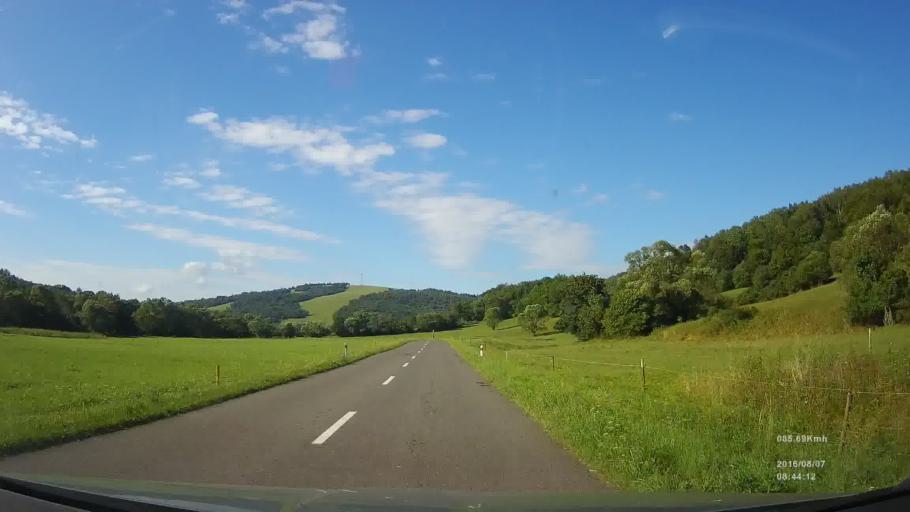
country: SK
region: Presovsky
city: Stropkov
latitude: 49.2699
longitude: 21.7498
